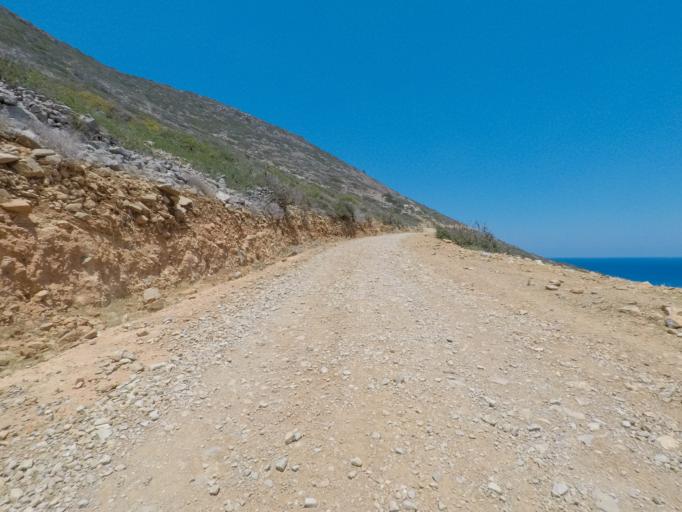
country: GR
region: Crete
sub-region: Nomos Lasithiou
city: Elounda
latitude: 35.3122
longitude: 25.7456
